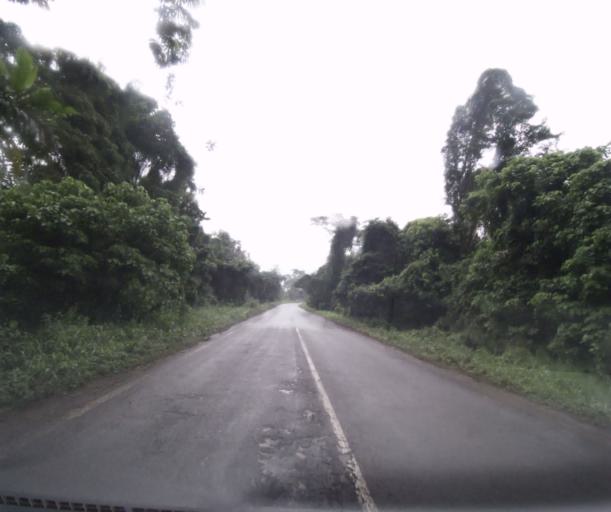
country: CM
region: Centre
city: Eseka
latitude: 3.8902
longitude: 10.7376
